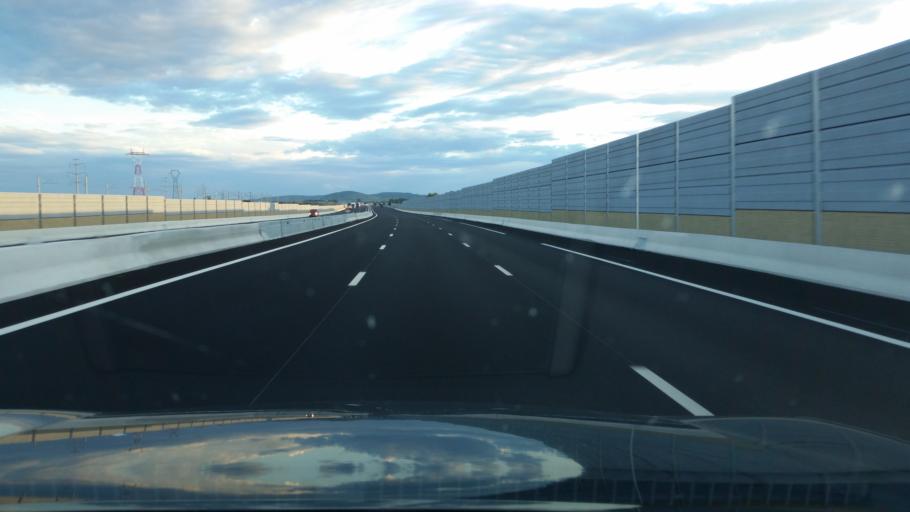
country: FR
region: Languedoc-Roussillon
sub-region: Departement de l'Herault
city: Lattes
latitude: 43.5872
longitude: 3.9037
